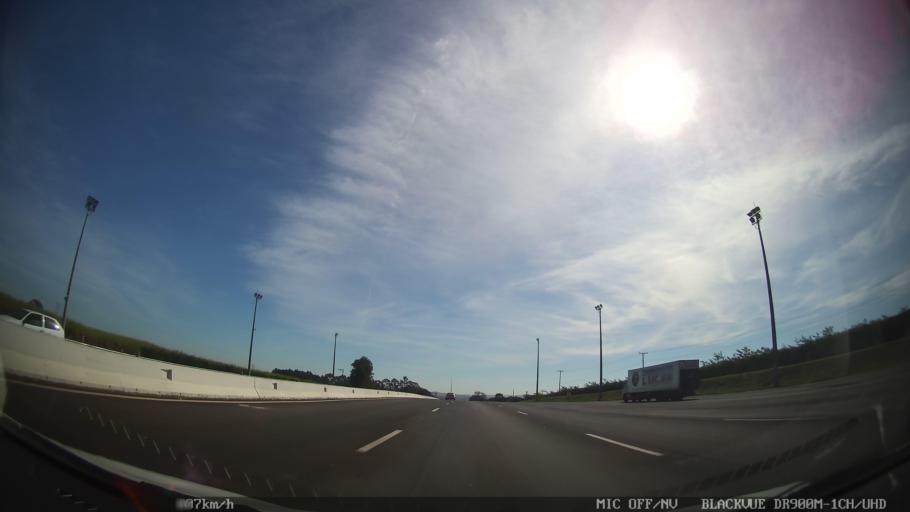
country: BR
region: Sao Paulo
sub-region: Leme
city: Leme
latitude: -22.2495
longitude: -47.3900
